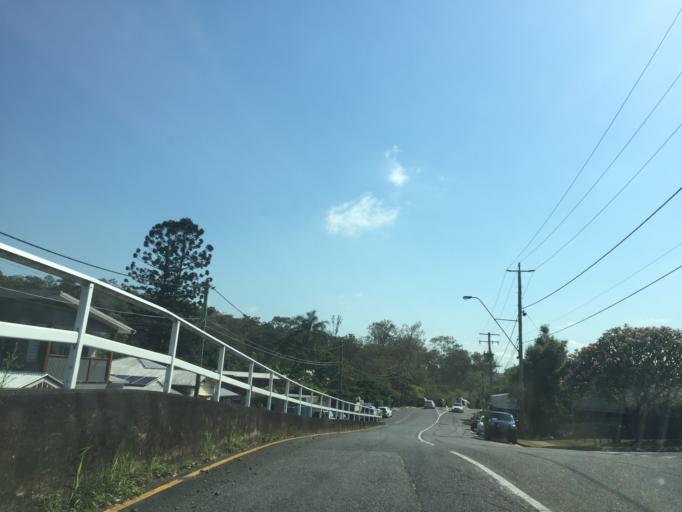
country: AU
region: Queensland
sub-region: Brisbane
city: Milton
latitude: -27.4669
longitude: 152.9888
